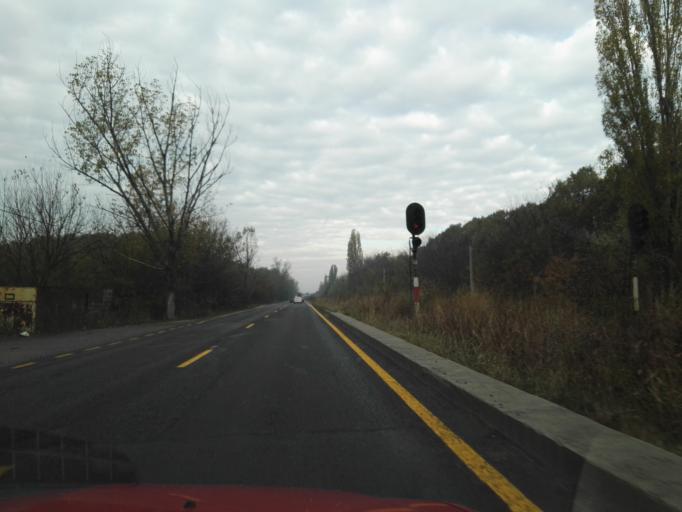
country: RO
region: Ilfov
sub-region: Comuna Magurele
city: Magurele
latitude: 44.3549
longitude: 26.0500
